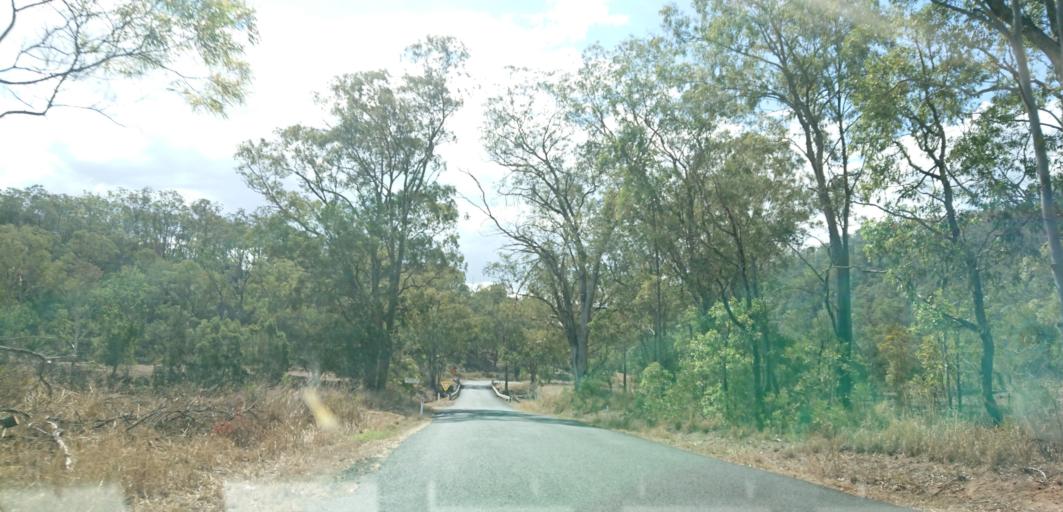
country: AU
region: Queensland
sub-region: Toowoomba
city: Top Camp
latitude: -27.7598
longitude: 152.0819
